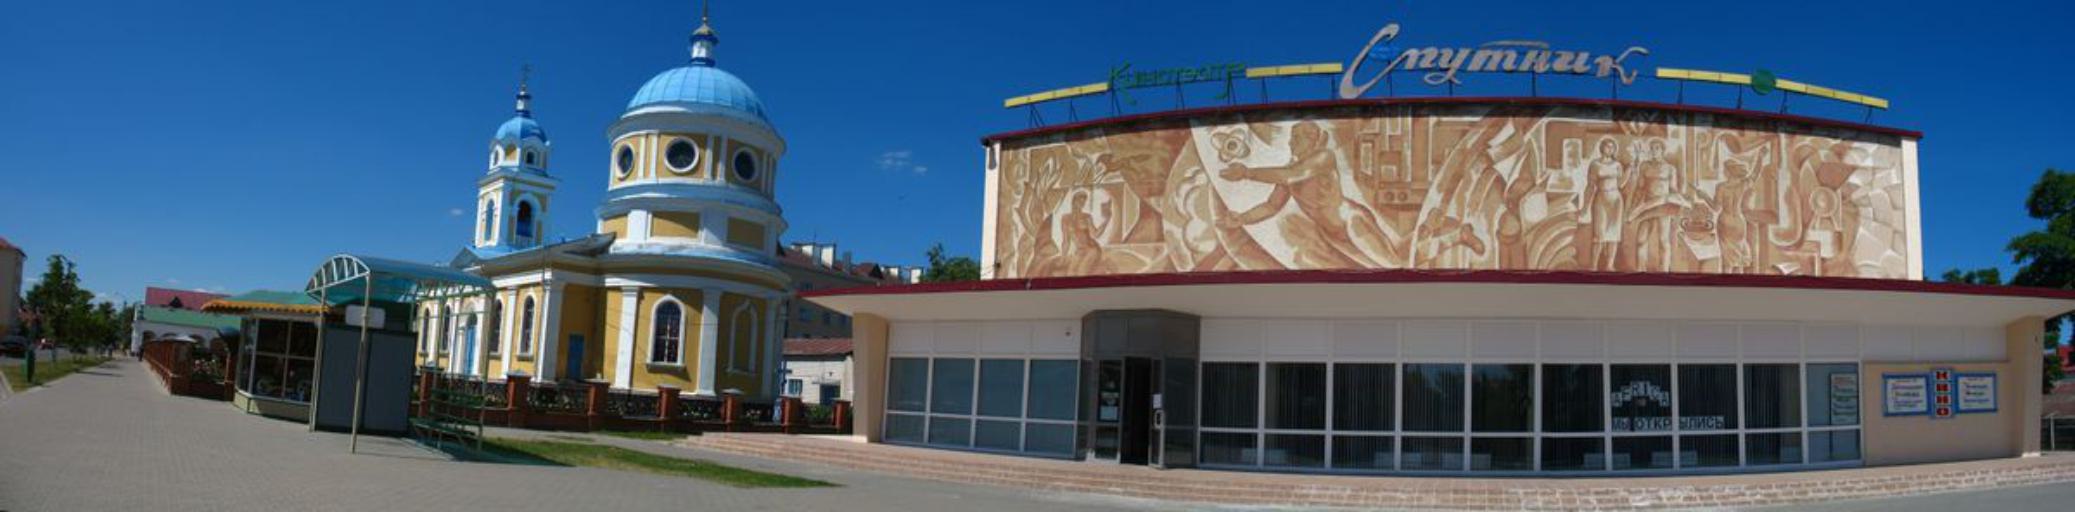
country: BY
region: Brest
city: Pruzhany
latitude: 52.5556
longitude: 24.4580
